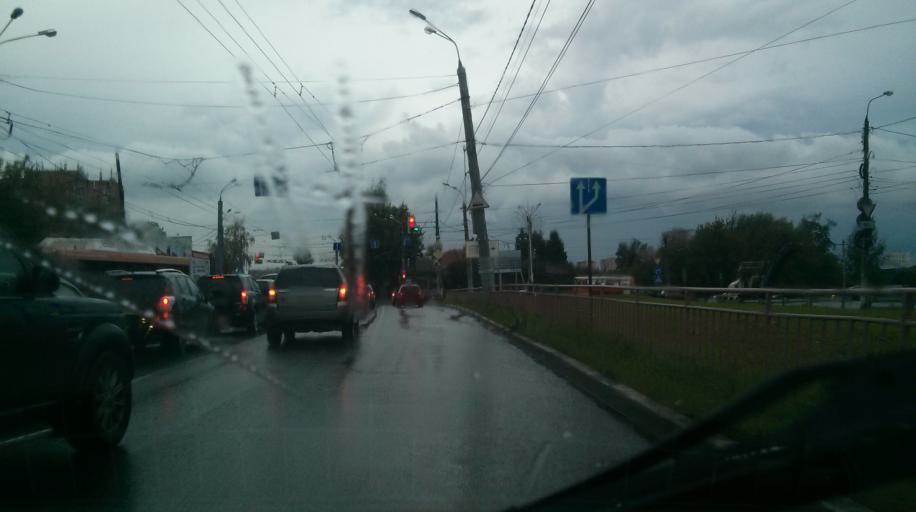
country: RU
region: Nizjnij Novgorod
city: Nizhniy Novgorod
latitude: 56.2995
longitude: 44.0325
